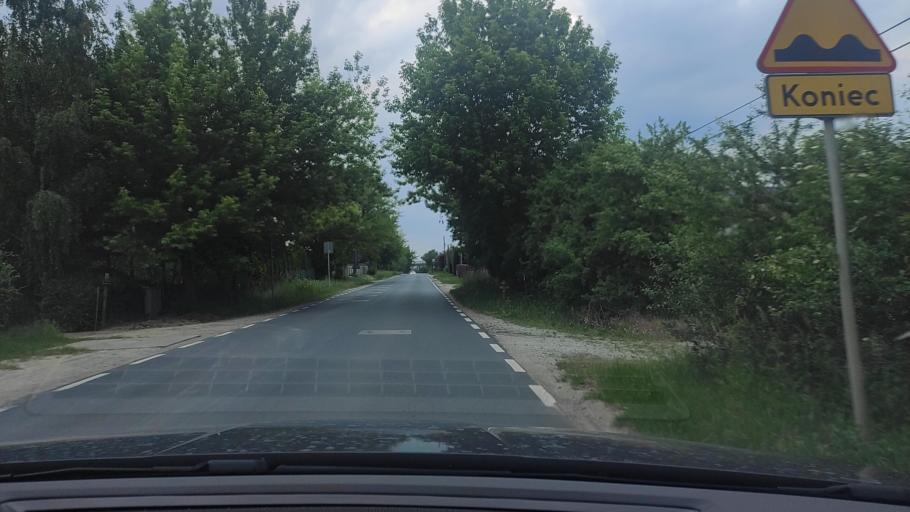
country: PL
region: Greater Poland Voivodeship
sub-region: Powiat poznanski
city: Kostrzyn
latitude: 52.4579
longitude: 17.1667
